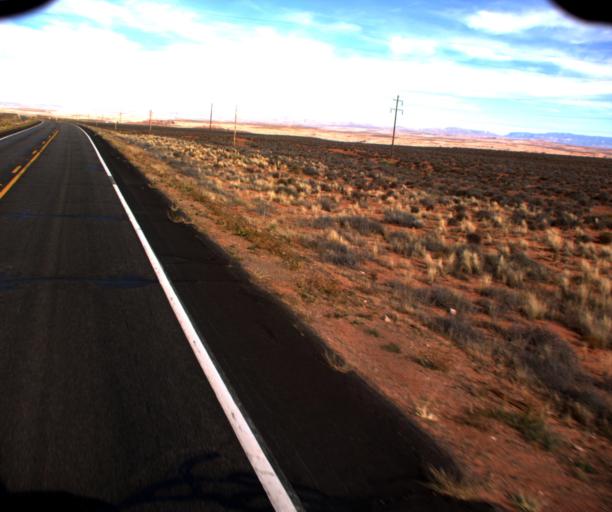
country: US
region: Arizona
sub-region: Navajo County
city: Kayenta
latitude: 36.9183
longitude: -109.7681
